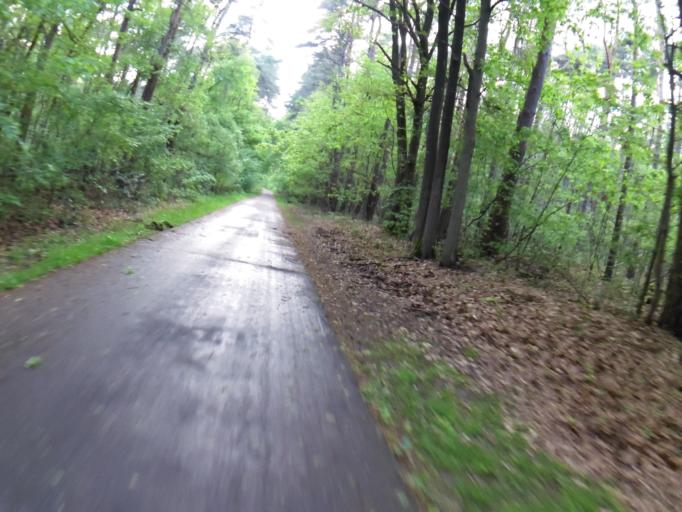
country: BE
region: Flanders
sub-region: Provincie Limburg
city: Zutendaal
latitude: 50.9464
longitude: 5.5444
